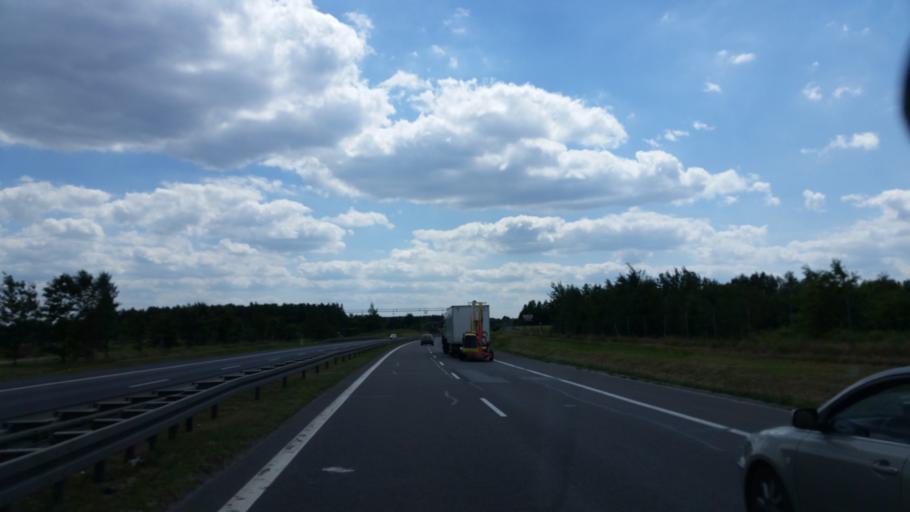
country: PL
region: Masovian Voivodeship
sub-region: Powiat ostrowski
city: Ostrow Mazowiecka
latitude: 52.8104
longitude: 21.8771
